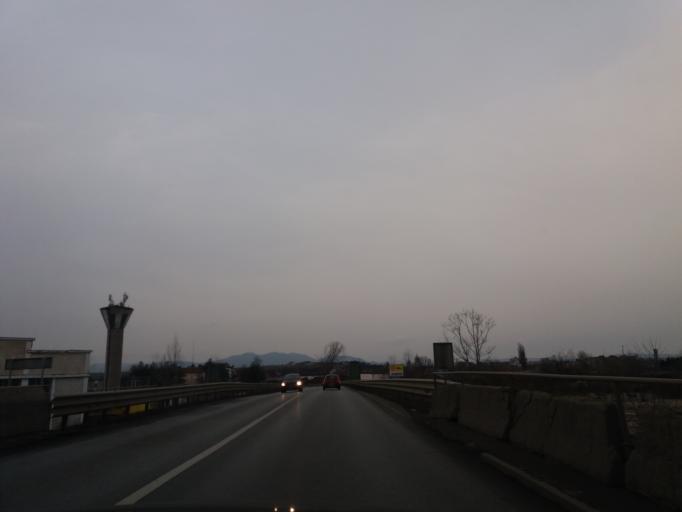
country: RO
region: Hunedoara
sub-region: Oras Simeria
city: Simeria
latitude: 45.8382
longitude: 23.0269
